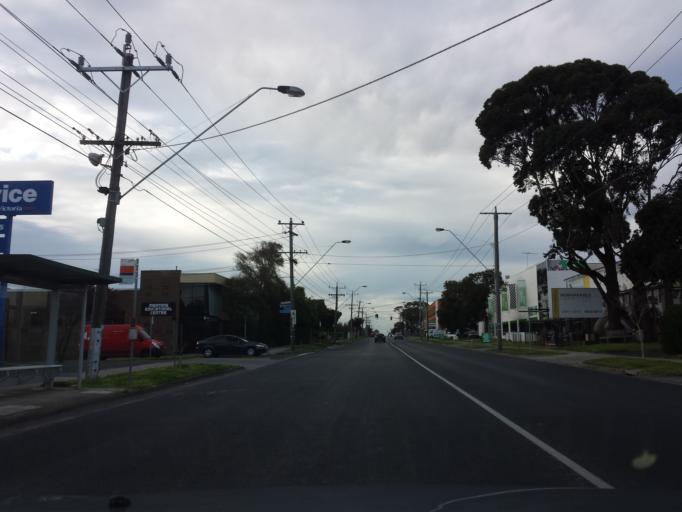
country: AU
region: Victoria
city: Highett
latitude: -37.9435
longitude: 145.0598
